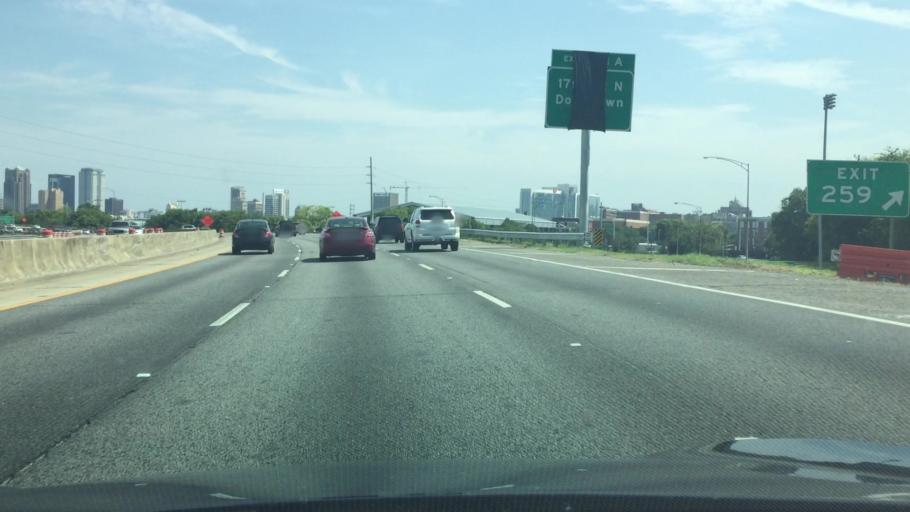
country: US
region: Alabama
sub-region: Jefferson County
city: Birmingham
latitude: 33.4973
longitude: -86.8150
